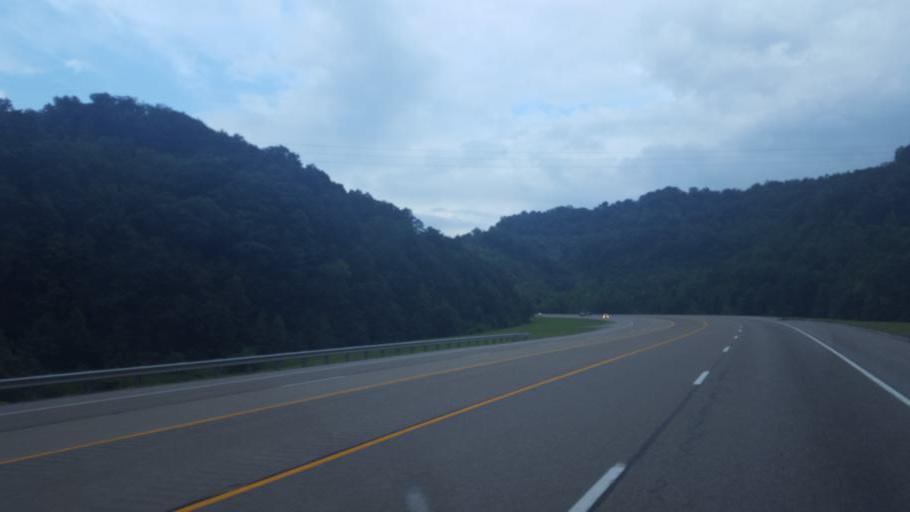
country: US
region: Kentucky
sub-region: Letcher County
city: Jenkins
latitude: 37.2208
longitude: -82.6269
